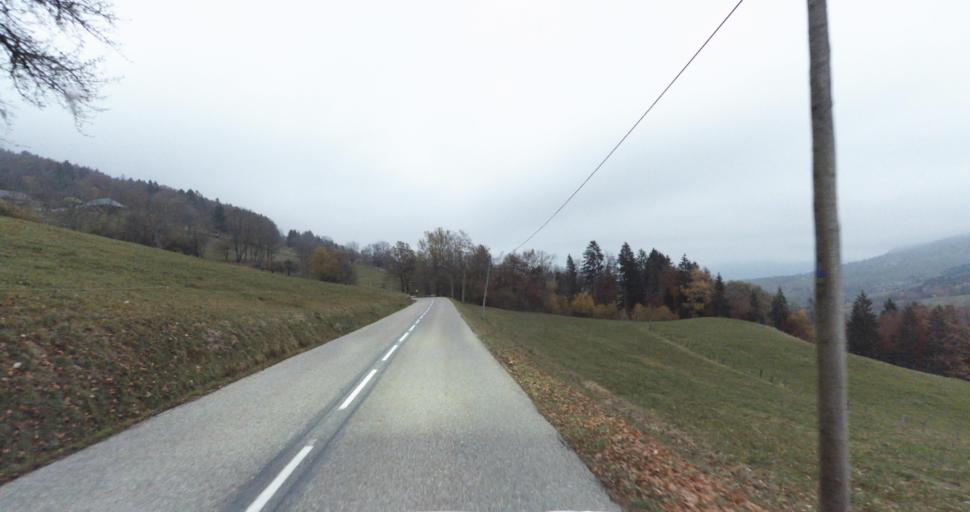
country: FR
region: Rhone-Alpes
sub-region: Departement de la Haute-Savoie
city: Saint-Jorioz
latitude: 45.7866
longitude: 6.1336
